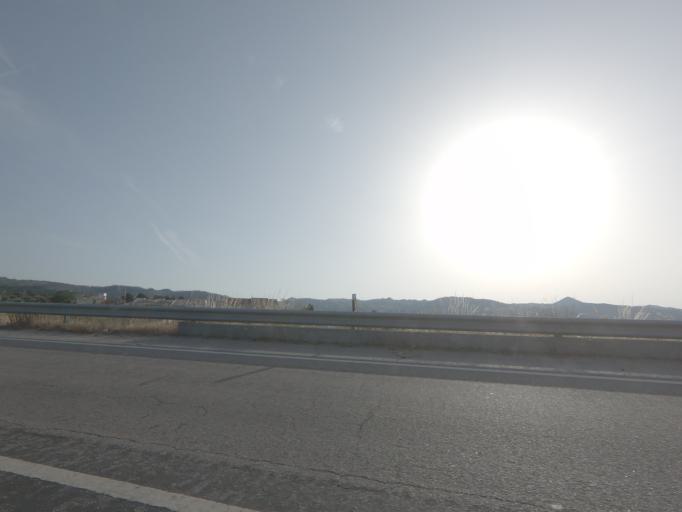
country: PT
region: Vila Real
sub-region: Sabrosa
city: Sabrosa
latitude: 41.2784
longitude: -7.4717
